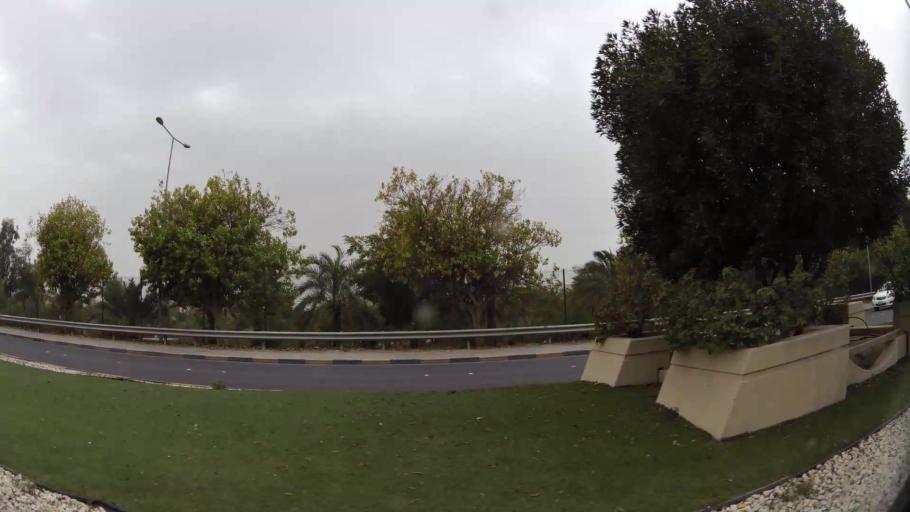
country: BH
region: Northern
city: Ar Rifa'
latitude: 26.1406
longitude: 50.5431
